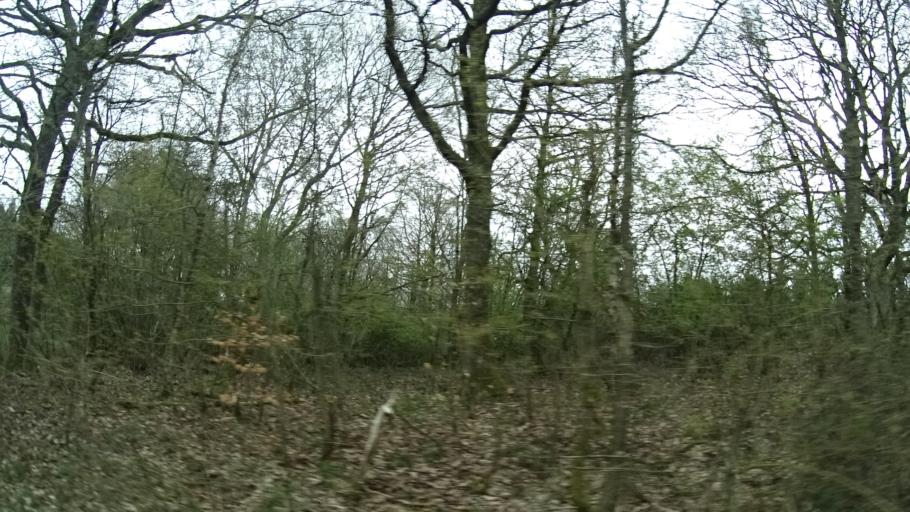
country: DE
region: Rheinland-Pfalz
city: Gerach
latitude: 49.7512
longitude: 7.3210
